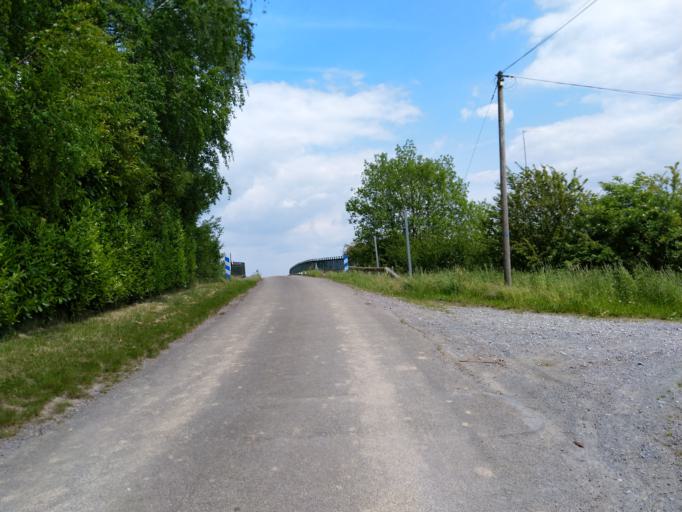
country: FR
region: Nord-Pas-de-Calais
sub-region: Departement du Nord
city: Le Quesnoy
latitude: 50.2465
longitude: 3.6554
